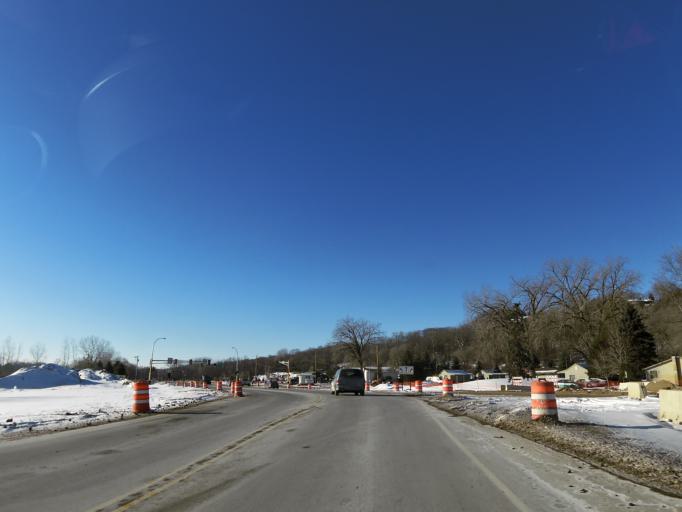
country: US
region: Minnesota
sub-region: Scott County
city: Shakopee
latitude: 44.8118
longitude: -93.5408
